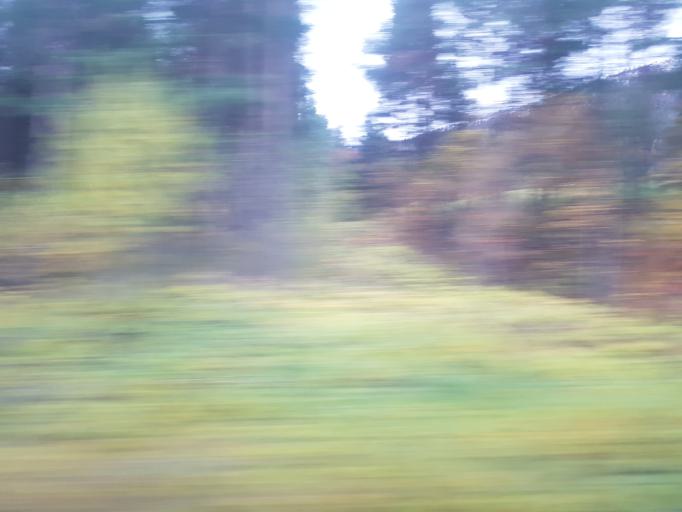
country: NO
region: Oppland
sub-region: Dovre
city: Dovre
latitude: 61.9174
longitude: 9.3440
